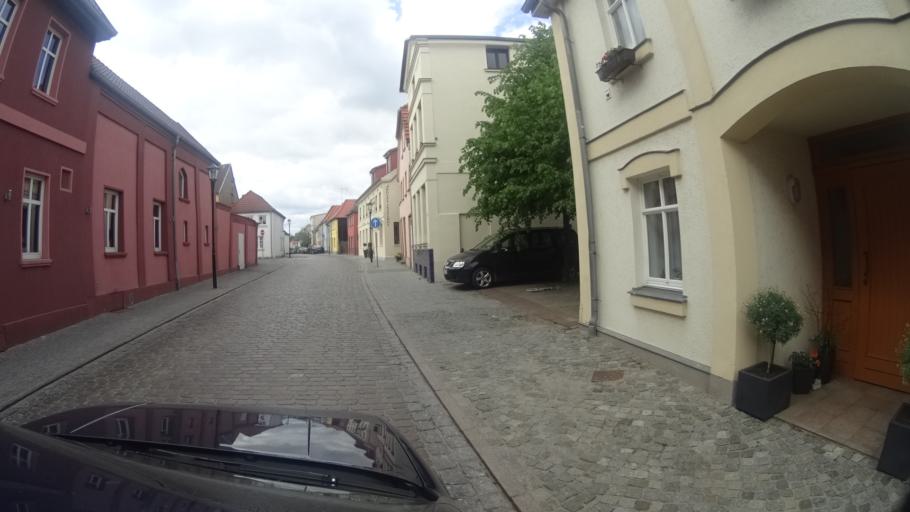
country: DE
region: Mecklenburg-Vorpommern
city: Malchow
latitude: 53.4755
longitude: 12.4325
